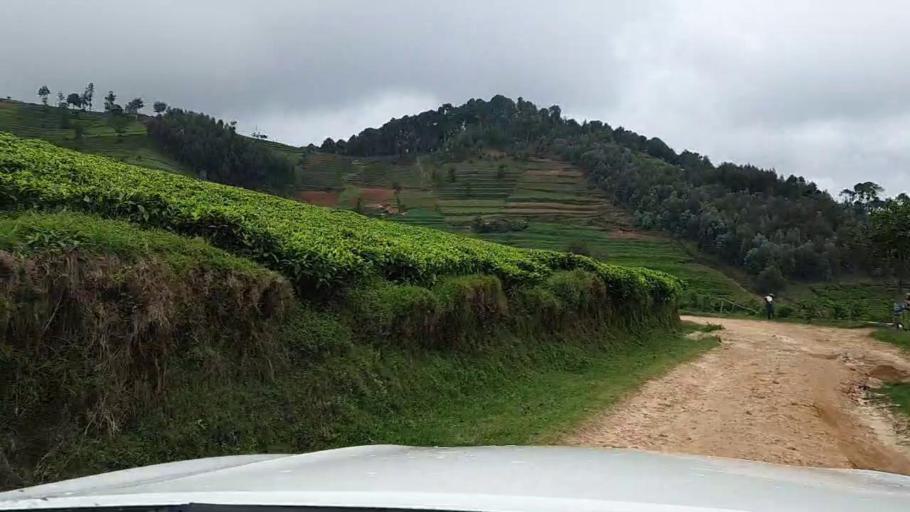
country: RW
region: Western Province
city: Kibuye
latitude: -2.2871
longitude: 29.3781
